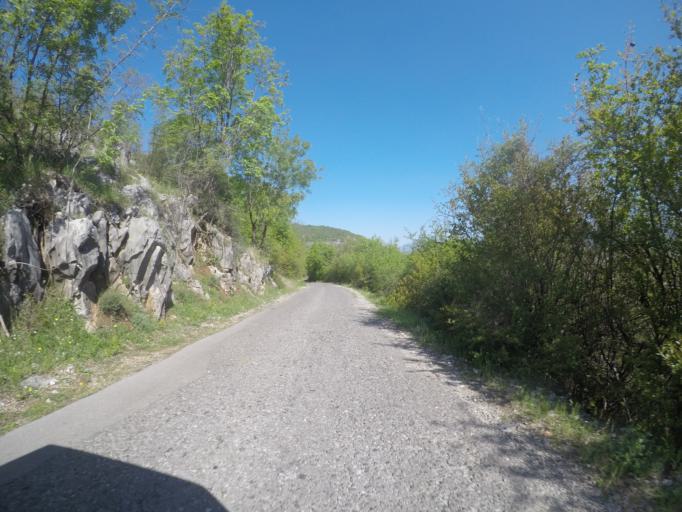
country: ME
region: Danilovgrad
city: Danilovgrad
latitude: 42.5294
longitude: 19.0923
